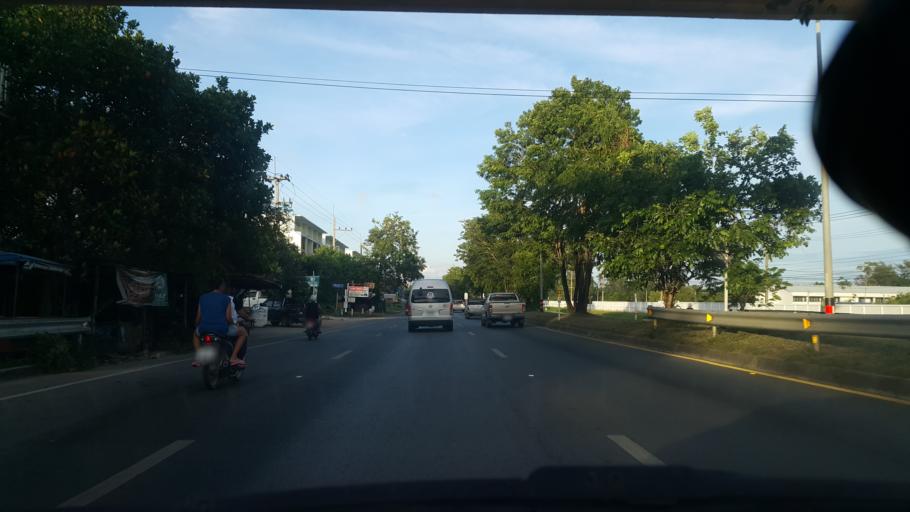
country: TH
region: Chon Buri
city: Sattahip
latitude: 12.6666
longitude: 100.9441
